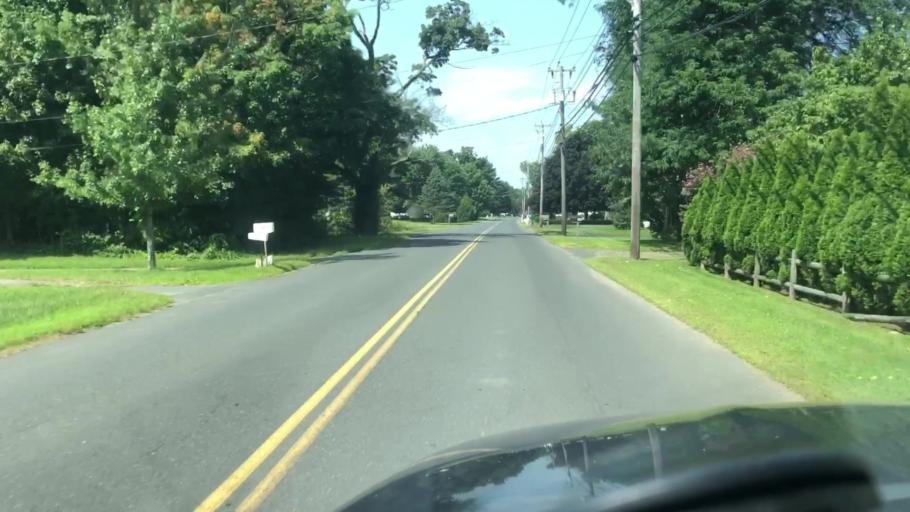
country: US
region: Massachusetts
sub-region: Hampden County
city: Westfield
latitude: 42.1411
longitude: -72.6995
